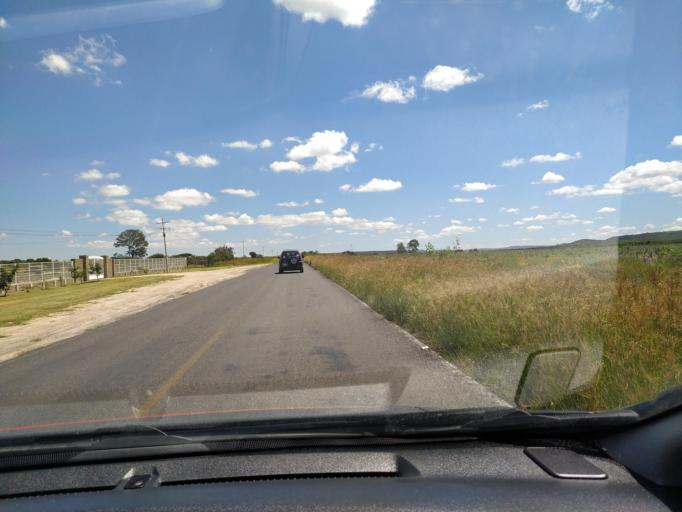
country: MX
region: Jalisco
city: San Diego de Alejandria
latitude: 21.0055
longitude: -102.0624
